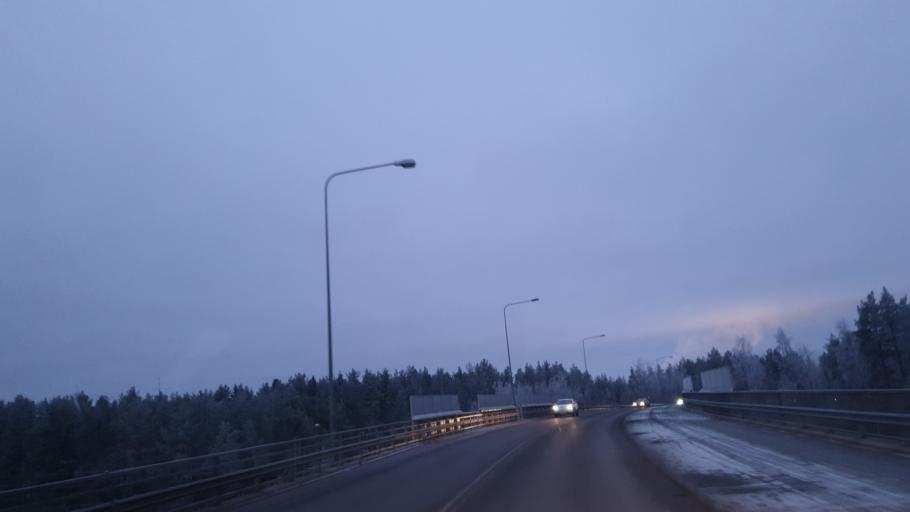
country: FI
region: Southern Ostrobothnia
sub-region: Seinaejoki
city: Nurmo
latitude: 62.7743
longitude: 22.8886
